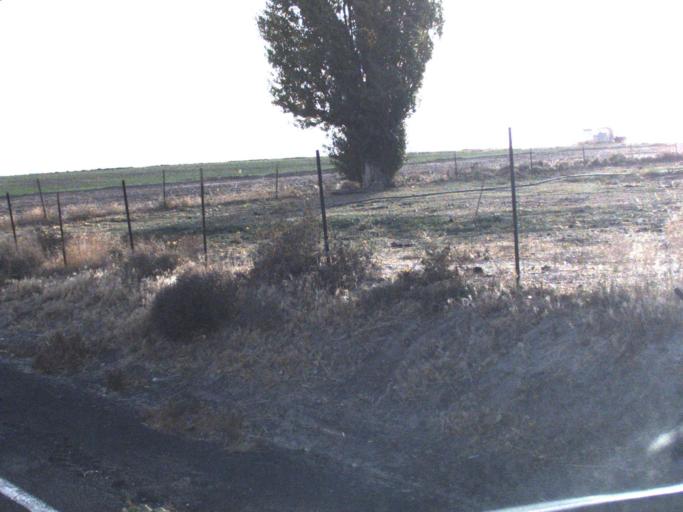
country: US
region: Washington
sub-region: Adams County
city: Ritzville
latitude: 47.2429
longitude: -118.6861
